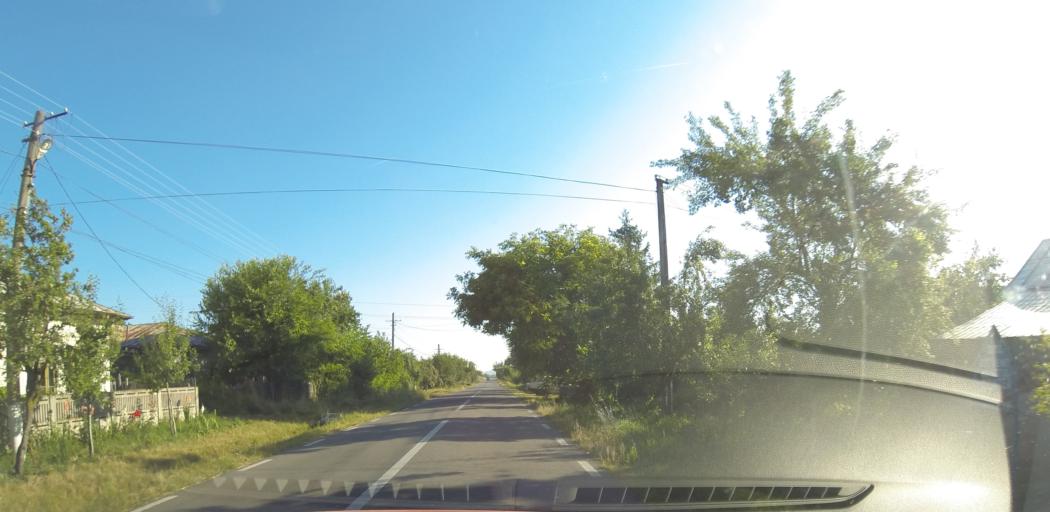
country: RO
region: Valcea
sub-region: Comuna Lacusteni
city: Lacusteni
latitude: 44.6989
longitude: 23.8987
